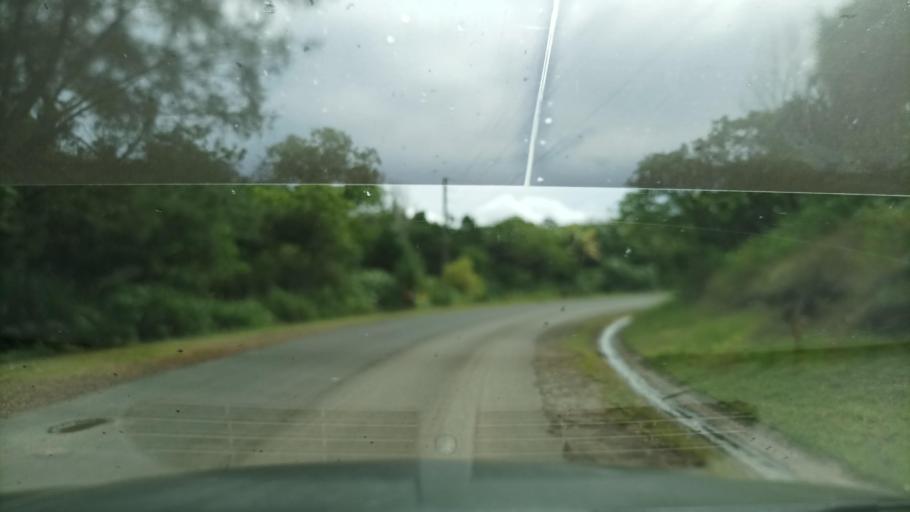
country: FM
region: Yap
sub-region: Weloy Municipality
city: Colonia
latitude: 9.5483
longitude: 138.1592
